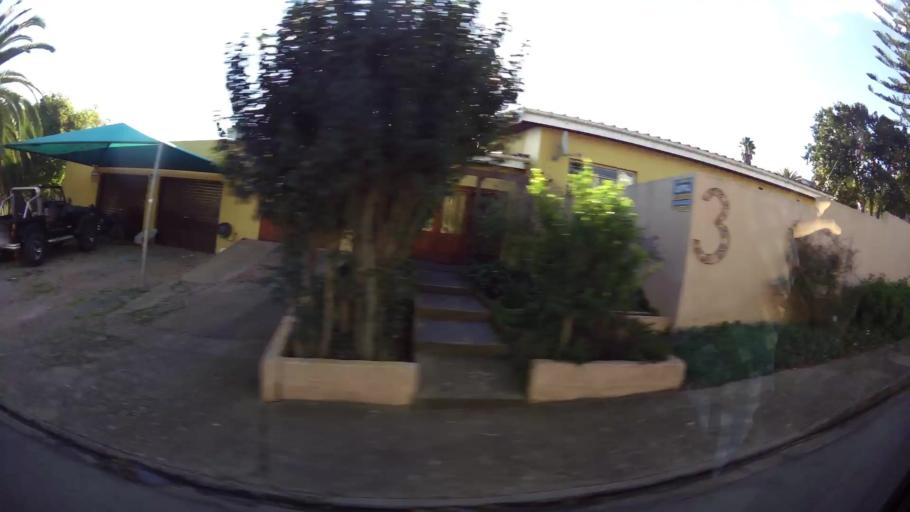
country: ZA
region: Western Cape
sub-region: Eden District Municipality
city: Riversdale
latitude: -34.0879
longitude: 20.9587
